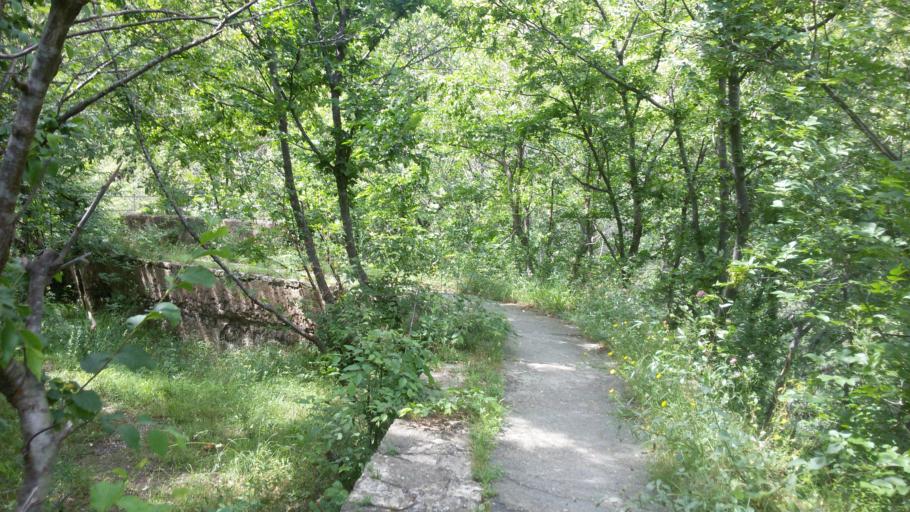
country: IT
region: Liguria
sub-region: Provincia di Genova
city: Piccarello
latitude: 44.4479
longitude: 8.9580
